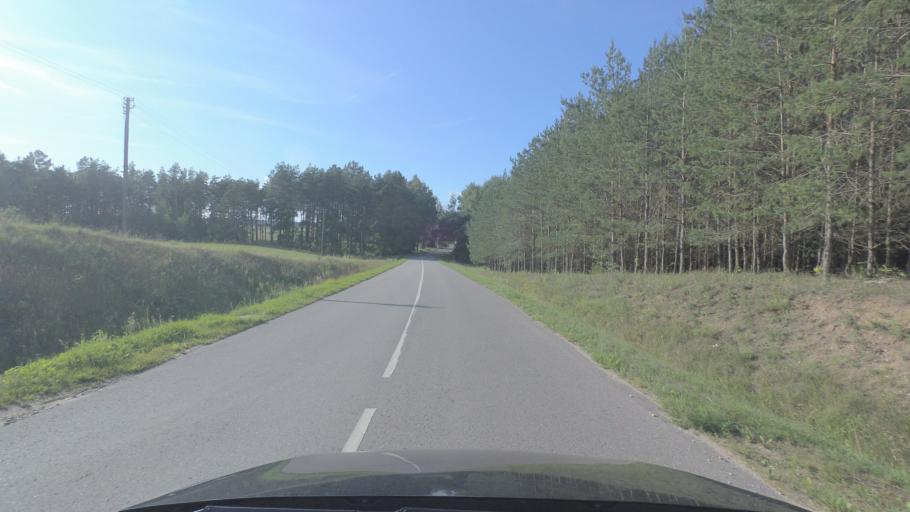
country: LT
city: Pabrade
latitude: 55.0933
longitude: 25.6842
